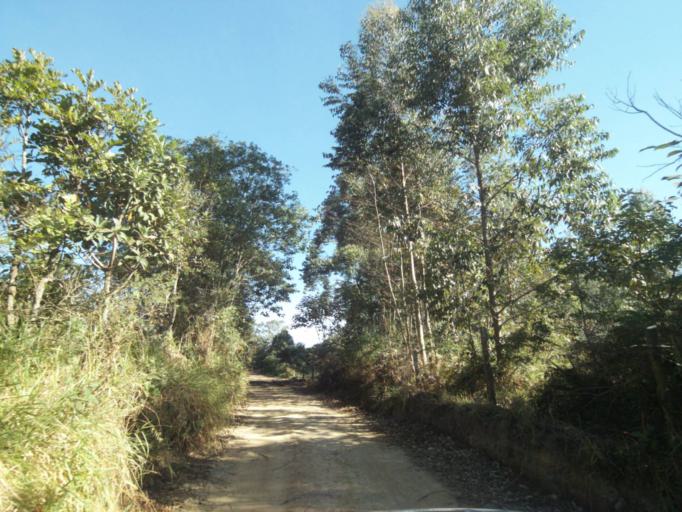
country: BR
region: Parana
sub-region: Tibagi
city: Tibagi
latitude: -24.5719
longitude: -50.4731
